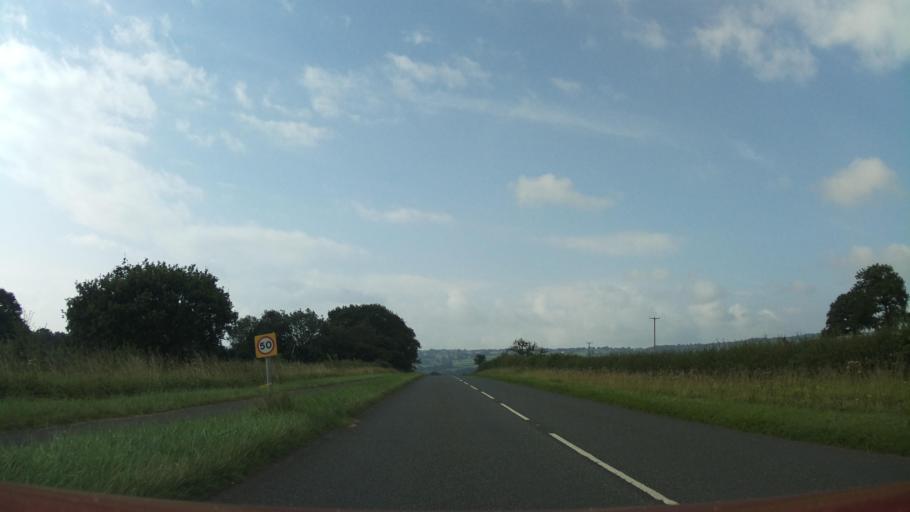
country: GB
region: England
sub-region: Bath and North East Somerset
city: Compton Martin
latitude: 51.3370
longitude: -2.6399
